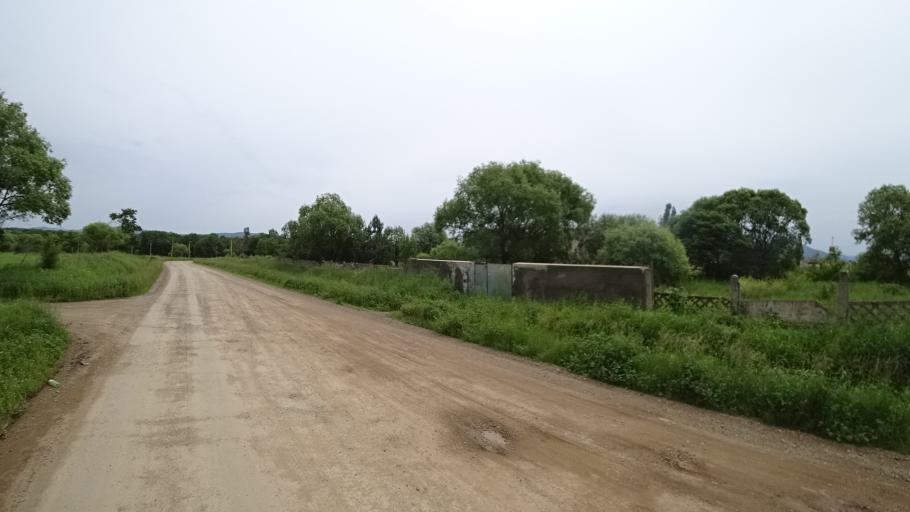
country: RU
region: Primorskiy
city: Novosysoyevka
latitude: 44.2024
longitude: 133.3134
